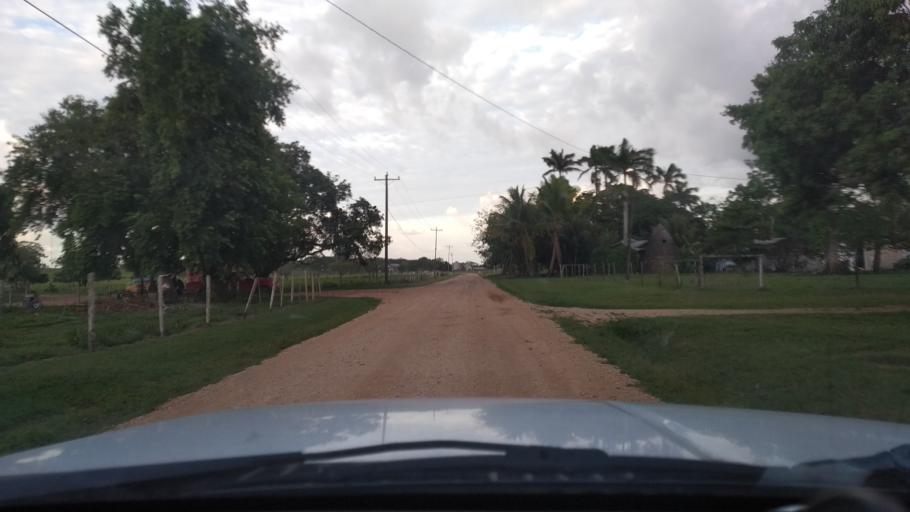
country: BZ
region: Cayo
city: San Ignacio
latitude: 17.2240
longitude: -88.9967
